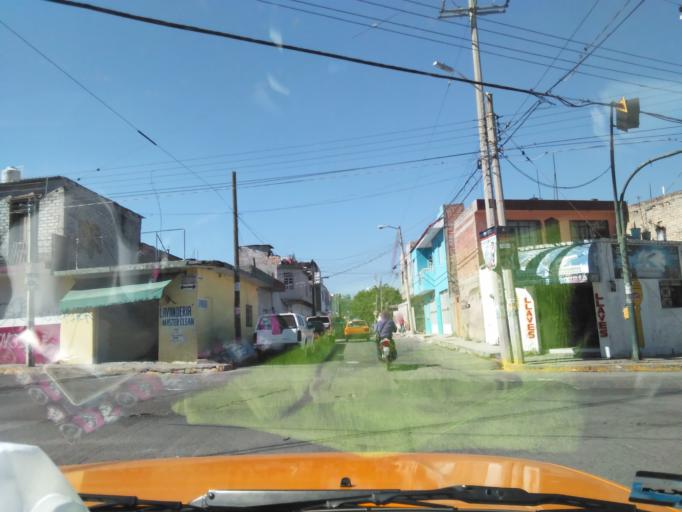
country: MX
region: Nayarit
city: Tepic
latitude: 21.4999
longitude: -104.8902
